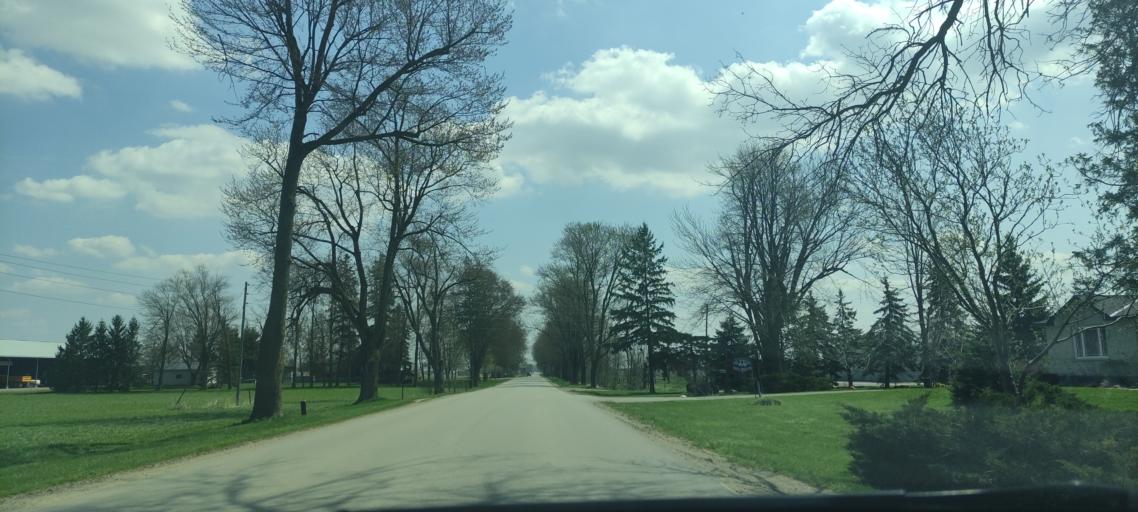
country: CA
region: Ontario
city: Stratford
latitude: 43.3348
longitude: -80.9768
